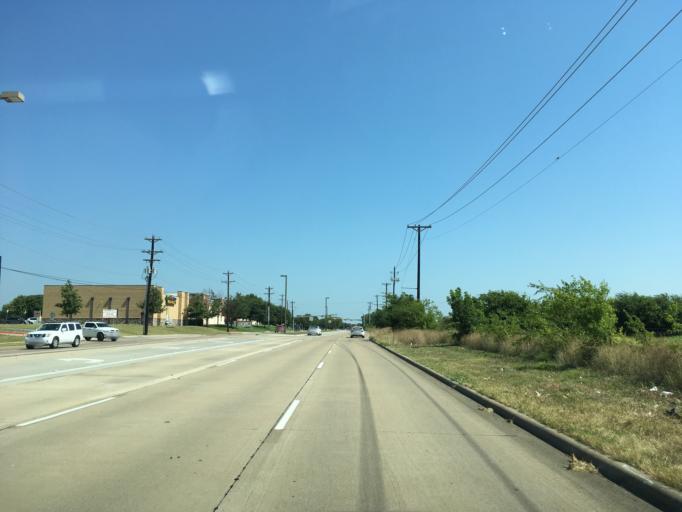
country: US
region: Texas
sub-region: Collin County
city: Fairview
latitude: 33.1562
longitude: -96.6806
